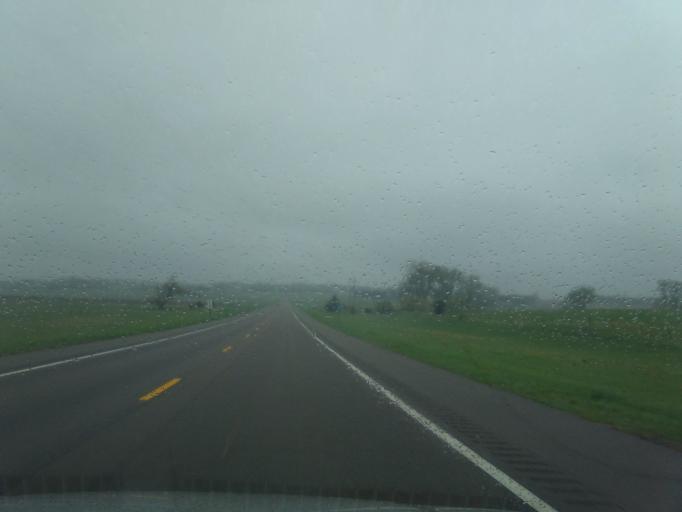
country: US
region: Nebraska
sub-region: Madison County
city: Norfolk
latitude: 42.0871
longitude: -97.3228
